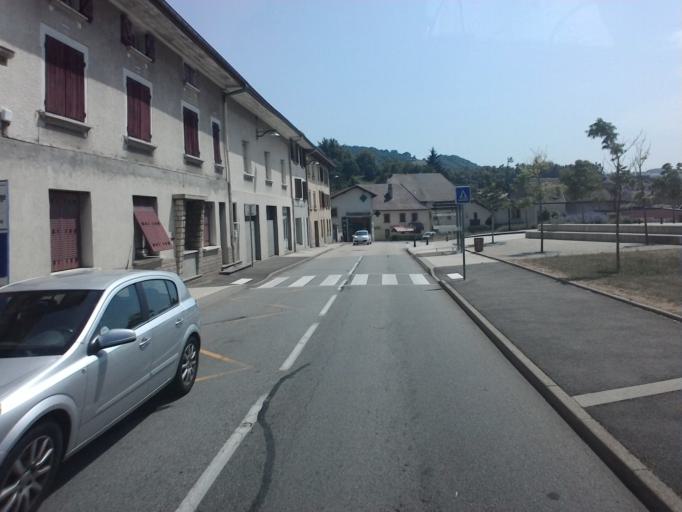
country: FR
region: Rhone-Alpes
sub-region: Departement de l'Isere
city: Montferrat
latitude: 45.4897
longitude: 5.5929
